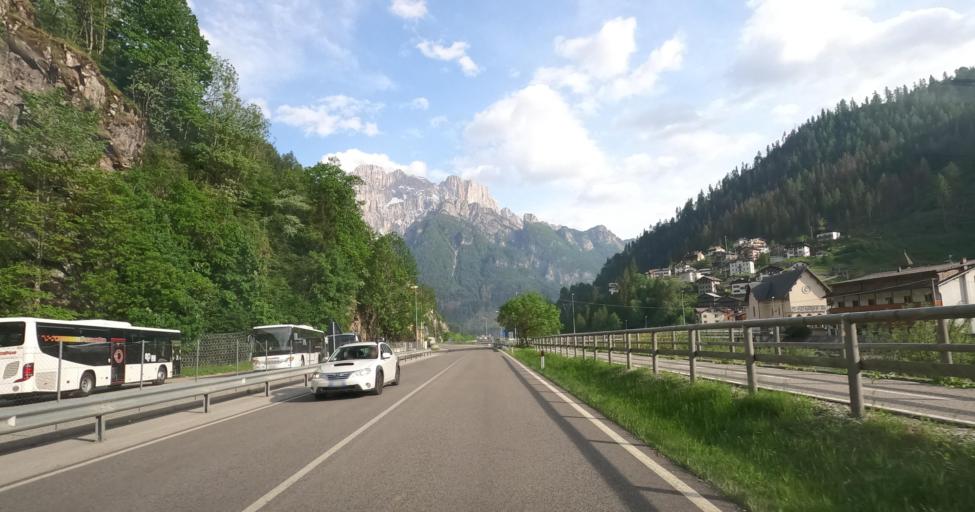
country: IT
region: Veneto
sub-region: Provincia di Belluno
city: Alleghe
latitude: 46.4233
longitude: 12.0086
